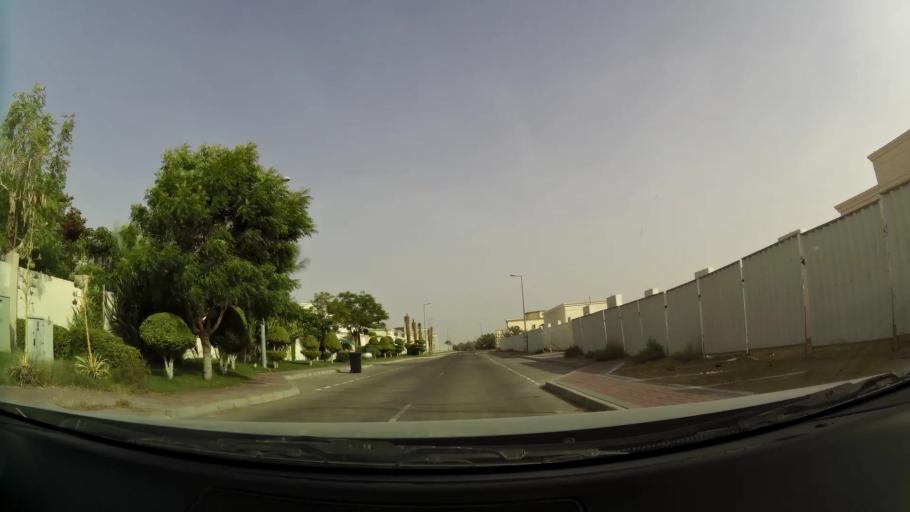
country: AE
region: Abu Dhabi
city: Al Ain
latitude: 24.1963
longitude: 55.6154
